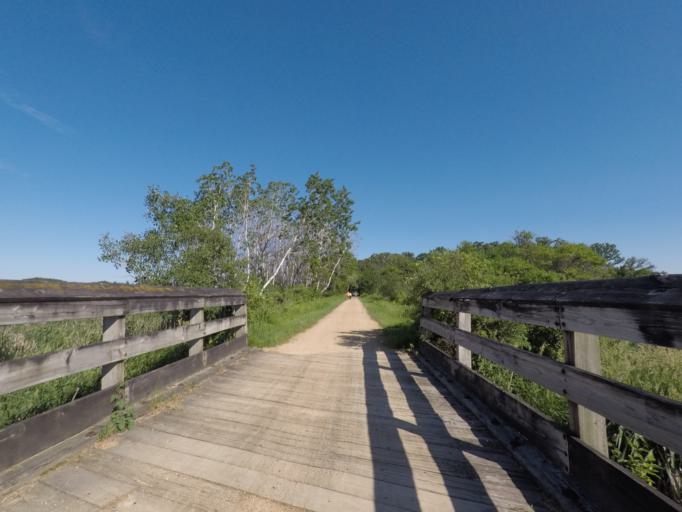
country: US
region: Wisconsin
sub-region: Dane County
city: Verona
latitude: 42.9839
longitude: -89.5640
